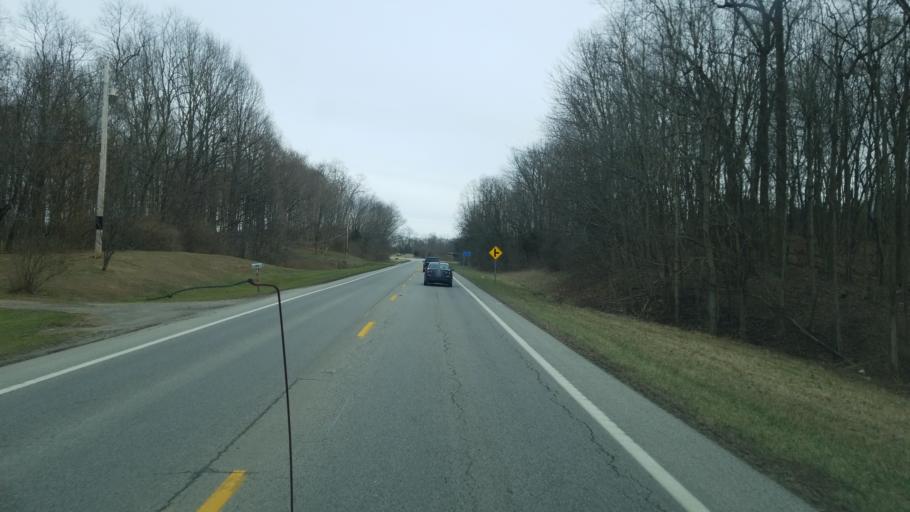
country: US
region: Ohio
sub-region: Highland County
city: Hillsboro
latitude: 39.1623
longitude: -83.6423
